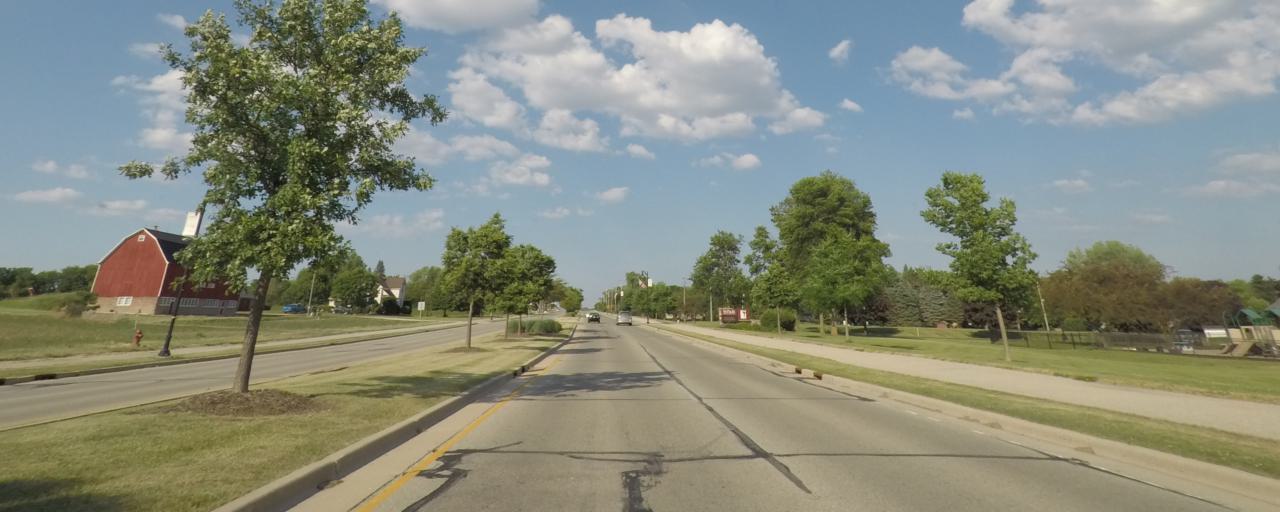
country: US
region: Wisconsin
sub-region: Milwaukee County
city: Hales Corners
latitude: 42.9253
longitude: -88.0920
